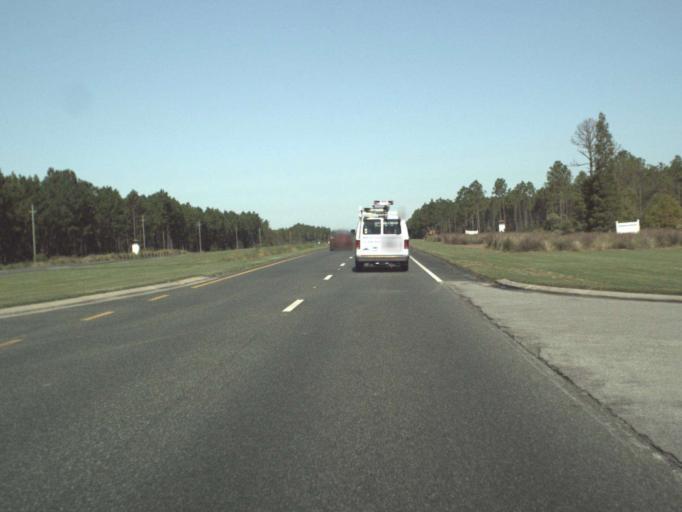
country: US
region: Florida
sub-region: Bay County
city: Laguna Beach
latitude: 30.2959
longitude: -86.0242
